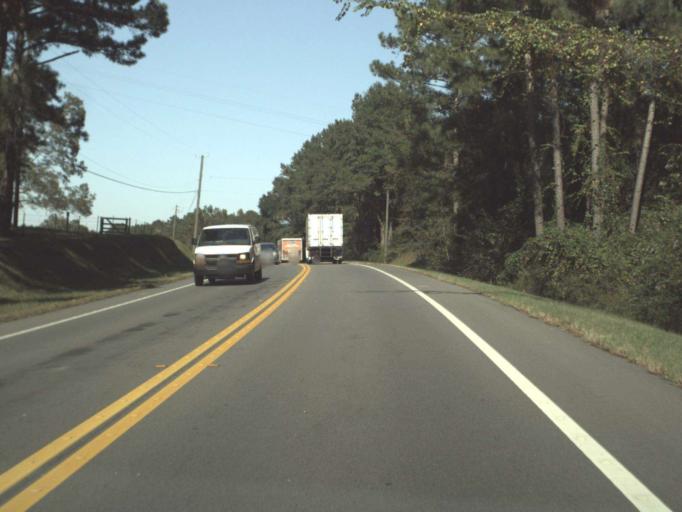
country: US
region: Alabama
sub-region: Covington County
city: Florala
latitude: 30.9842
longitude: -86.3413
